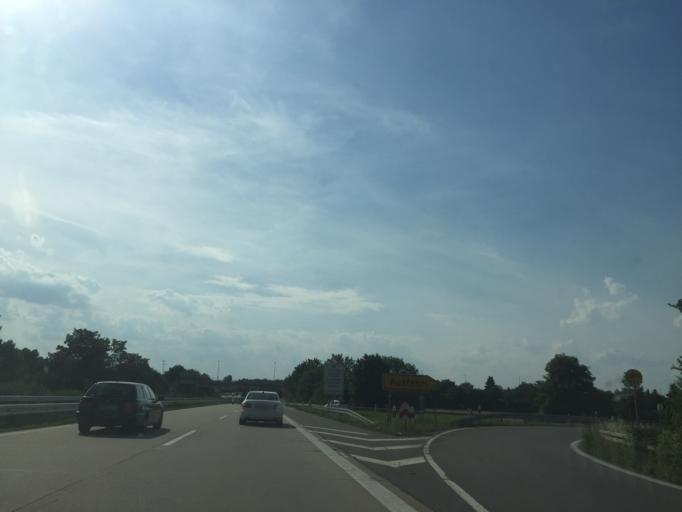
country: DE
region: Baden-Wuerttemberg
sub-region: Karlsruhe Region
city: Eppelheim
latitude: 49.4133
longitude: 8.6469
